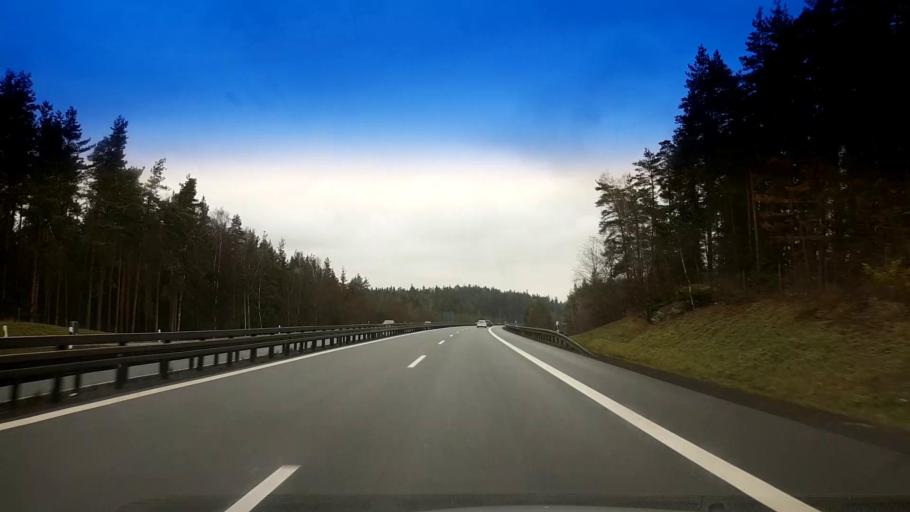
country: DE
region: Bavaria
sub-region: Upper Palatinate
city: Wiesau
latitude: 49.8600
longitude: 12.1803
